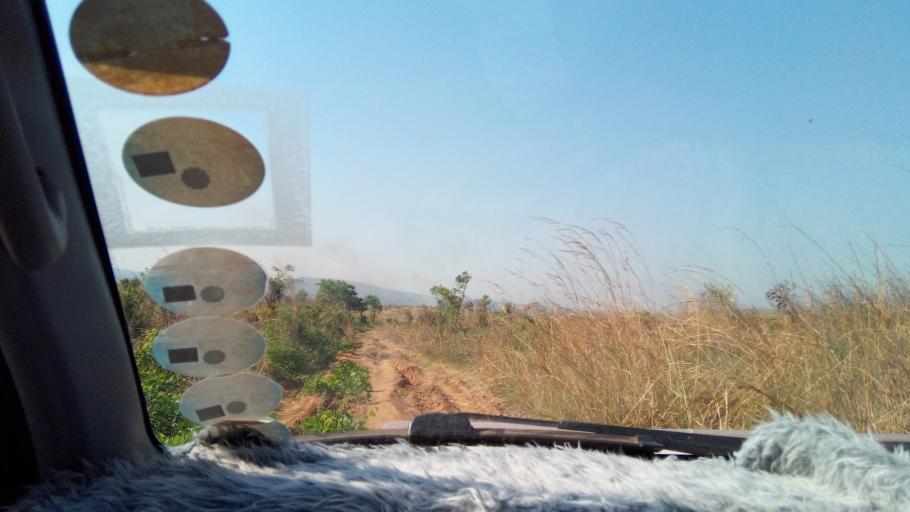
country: CD
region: Katanga
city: Kalemie
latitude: -5.9138
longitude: 29.1239
